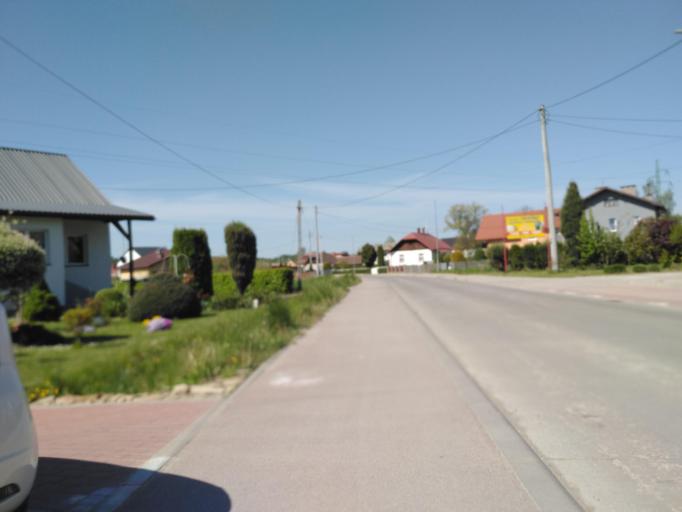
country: PL
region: Subcarpathian Voivodeship
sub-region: Powiat krosnienski
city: Korczyna
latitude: 49.6982
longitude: 21.8067
